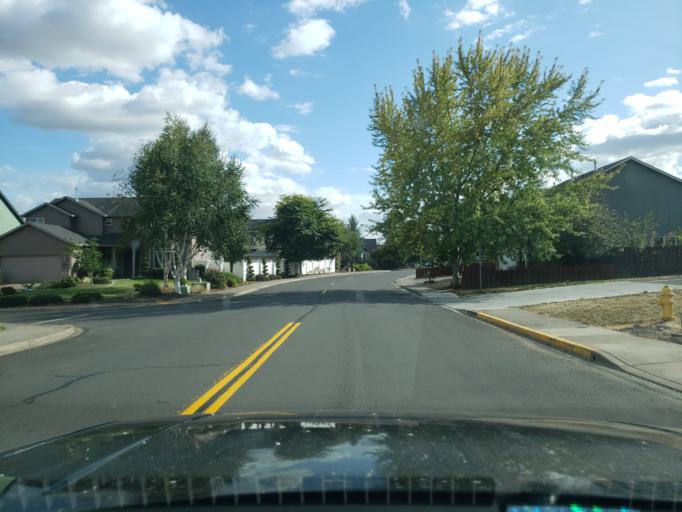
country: US
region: Oregon
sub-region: Yamhill County
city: McMinnville
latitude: 45.2105
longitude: -123.2193
